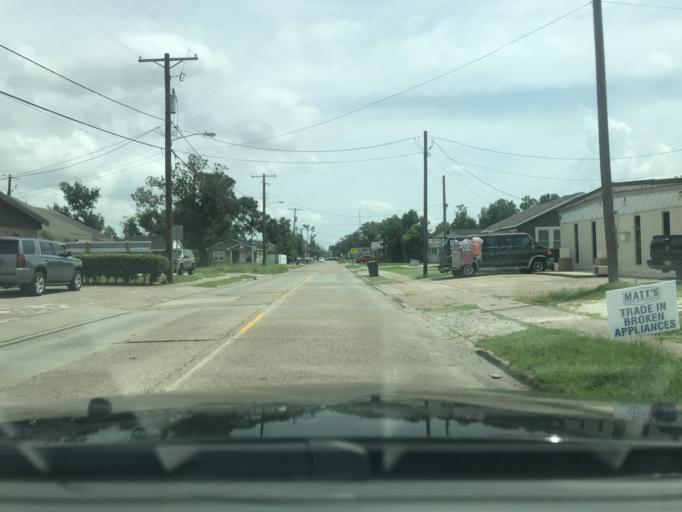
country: US
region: Louisiana
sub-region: Calcasieu Parish
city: Lake Charles
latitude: 30.2066
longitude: -93.2141
